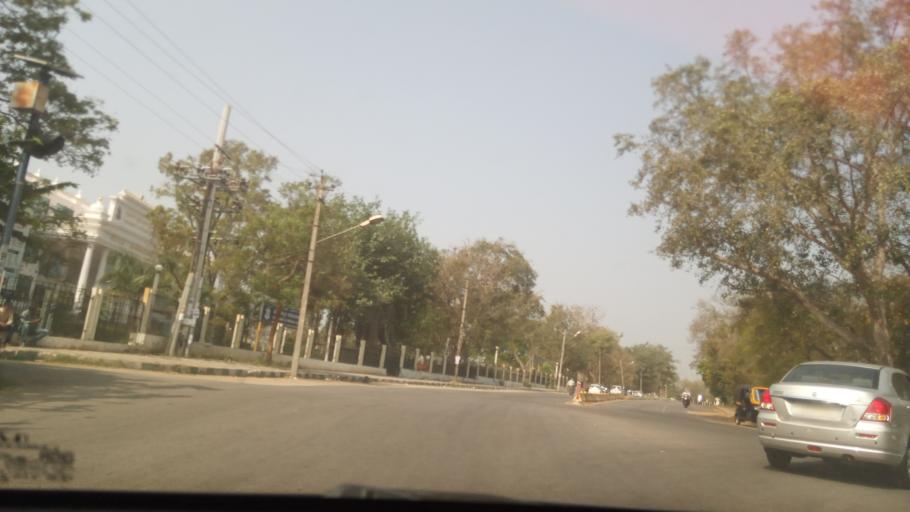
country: IN
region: Karnataka
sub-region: Mysore
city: Mysore
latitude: 12.3064
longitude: 76.6259
